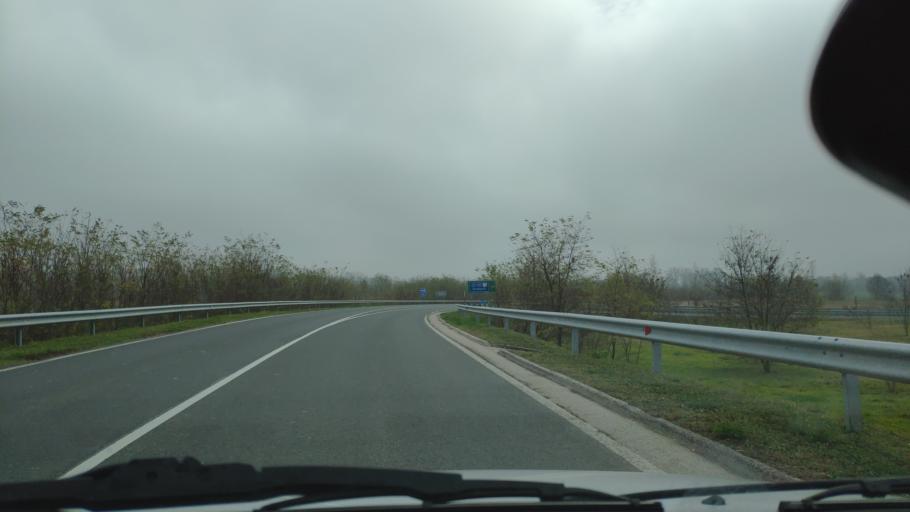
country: HU
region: Somogy
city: Balatonbereny
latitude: 46.6491
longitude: 17.2999
